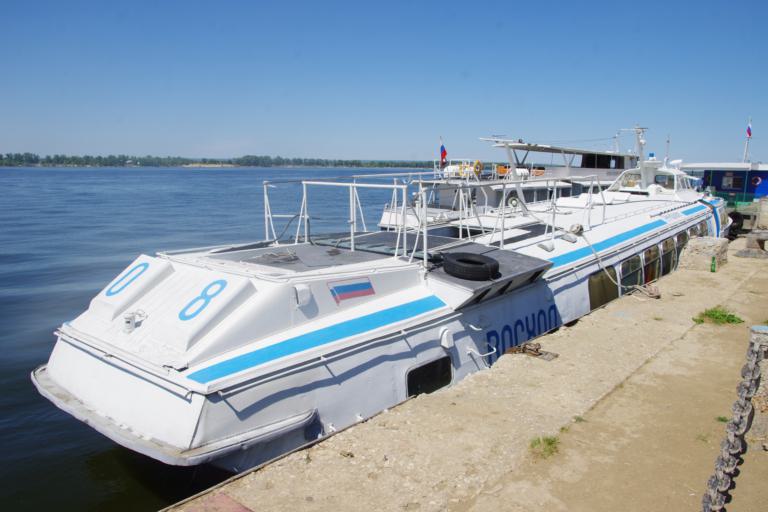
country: RU
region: Samara
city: Rozhdestveno
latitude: 53.1867
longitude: 50.0772
